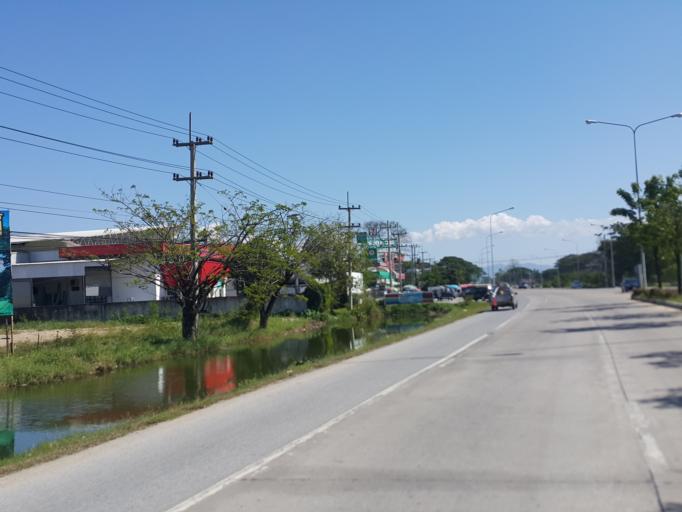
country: TH
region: Chiang Mai
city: Saraphi
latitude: 18.7624
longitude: 99.0402
